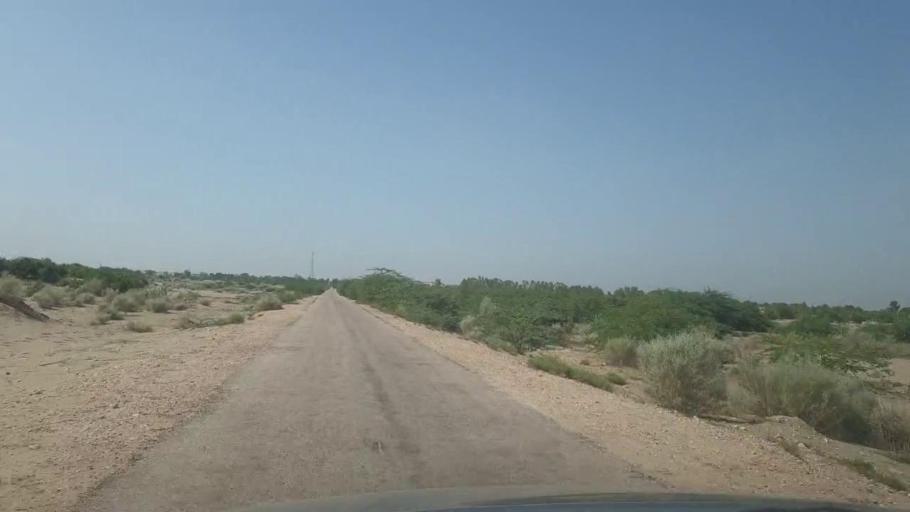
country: PK
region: Sindh
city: Rohri
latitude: 27.4181
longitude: 69.0800
